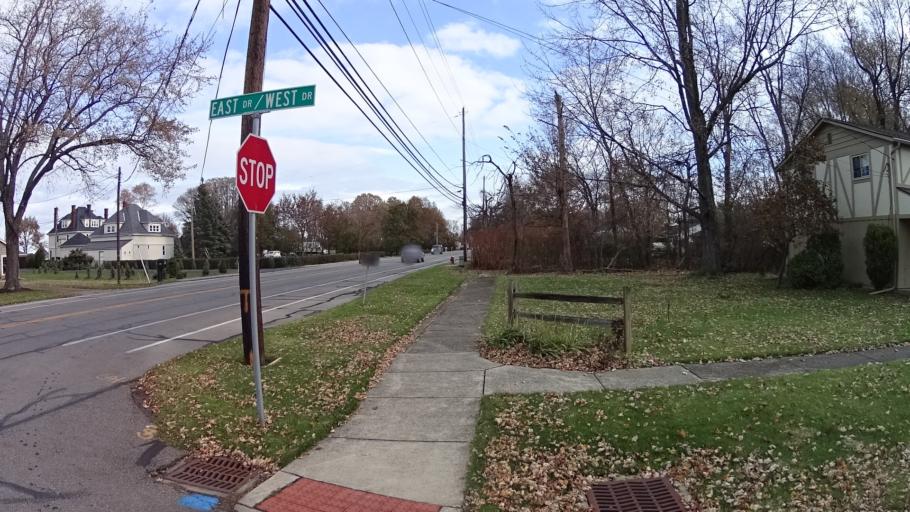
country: US
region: Ohio
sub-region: Lorain County
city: Sheffield Lake
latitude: 41.4874
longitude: -82.1196
